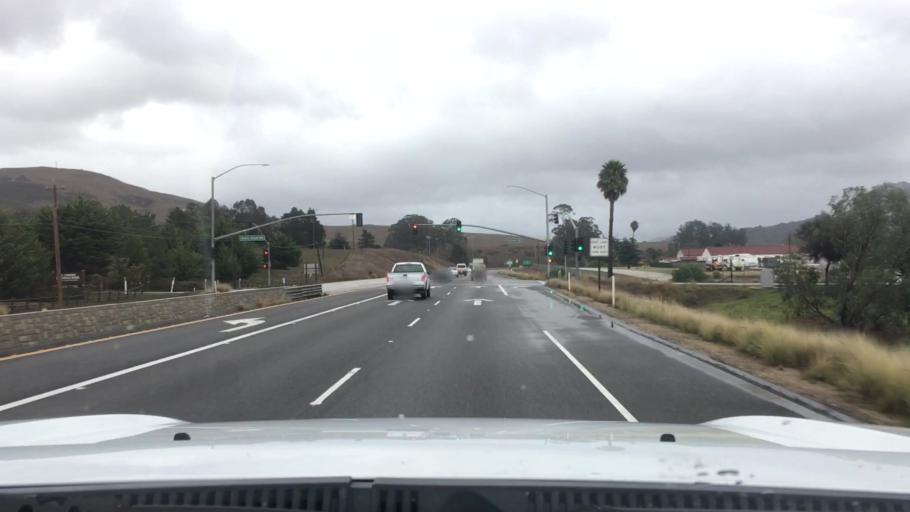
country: US
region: California
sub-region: San Luis Obispo County
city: San Luis Obispo
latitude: 35.3313
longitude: -120.7361
